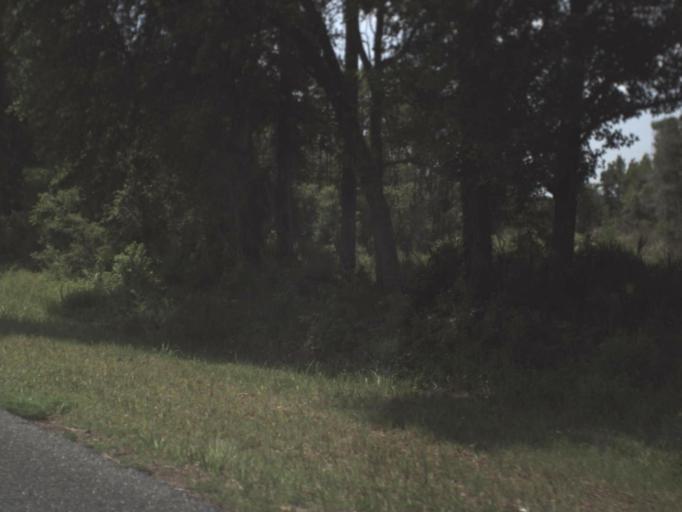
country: US
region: Florida
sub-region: Taylor County
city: Perry
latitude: 29.9532
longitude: -83.4601
